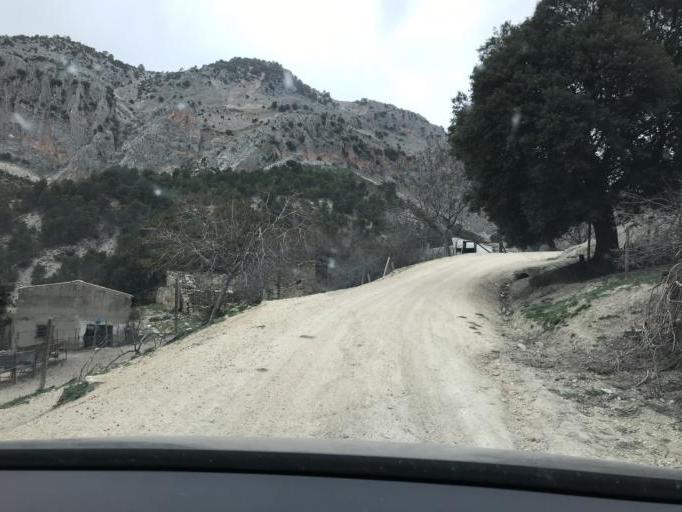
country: ES
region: Andalusia
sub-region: Provincia de Granada
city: Castril
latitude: 37.8812
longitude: -2.7538
